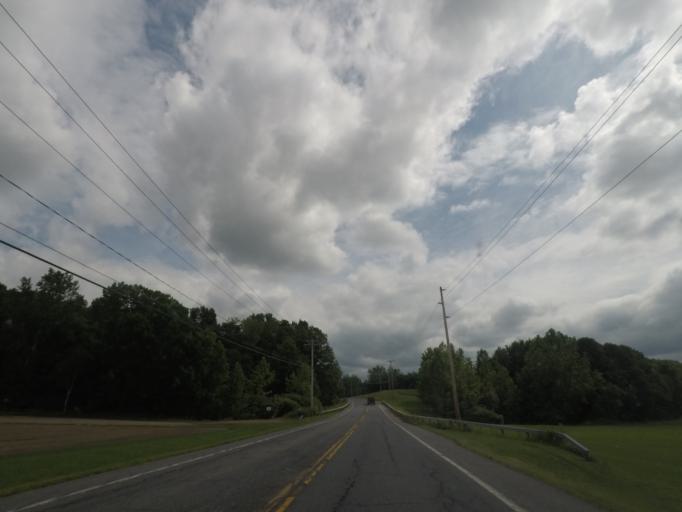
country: US
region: New York
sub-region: Saratoga County
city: Stillwater
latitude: 42.9192
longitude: -73.6306
